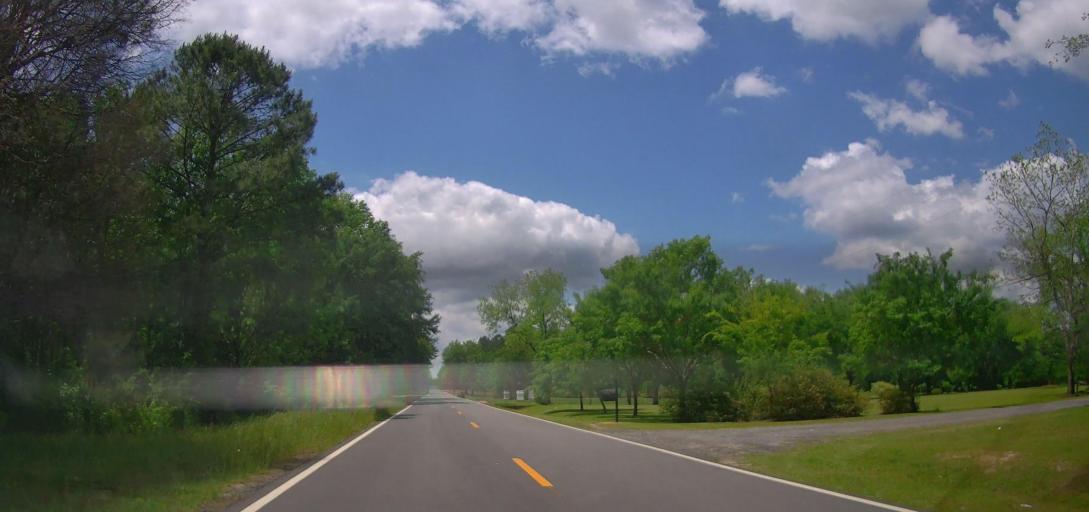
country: US
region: Georgia
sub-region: Laurens County
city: Dublin
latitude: 32.6007
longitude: -82.9151
